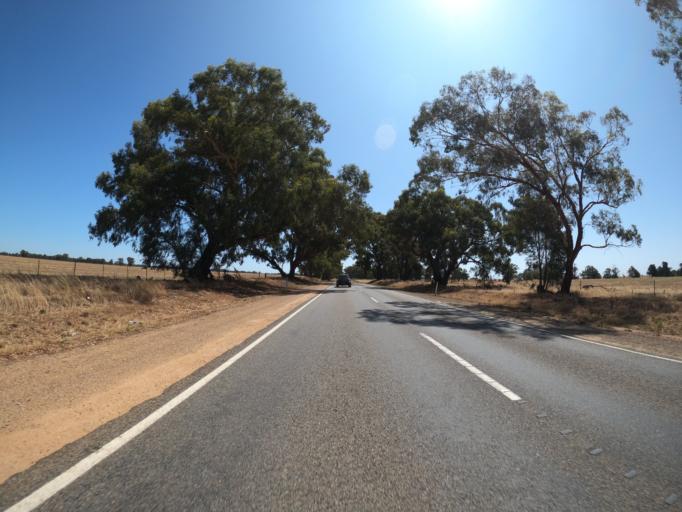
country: AU
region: Victoria
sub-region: Moira
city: Yarrawonga
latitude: -36.0242
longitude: 146.1105
